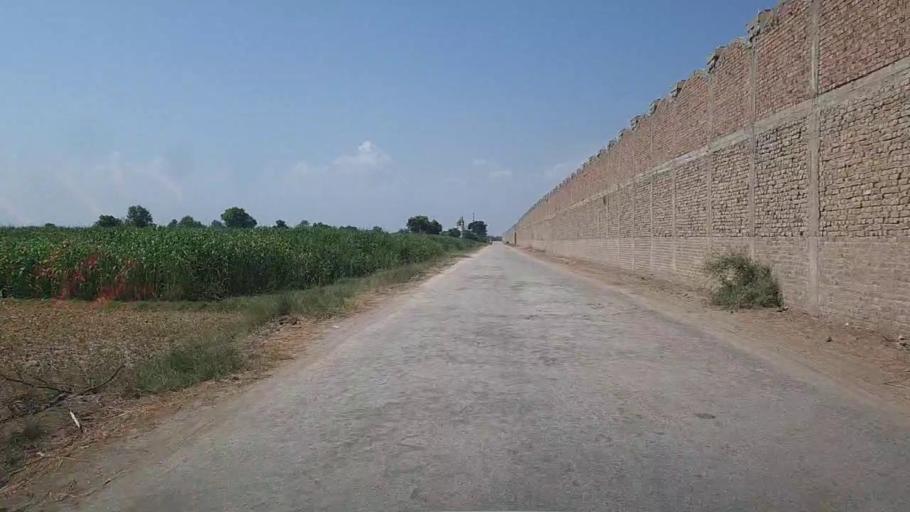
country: PK
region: Sindh
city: Khairpur
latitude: 28.0625
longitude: 69.6460
